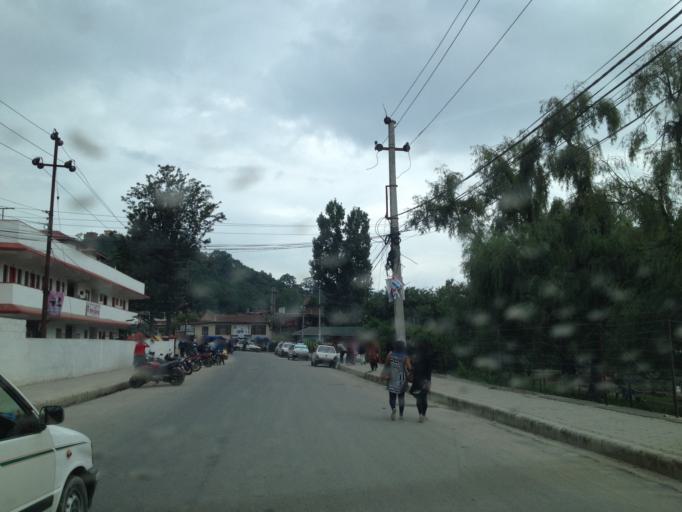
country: NP
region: Central Region
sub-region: Bagmati Zone
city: Kathmandu
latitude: 27.7096
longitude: 85.2896
